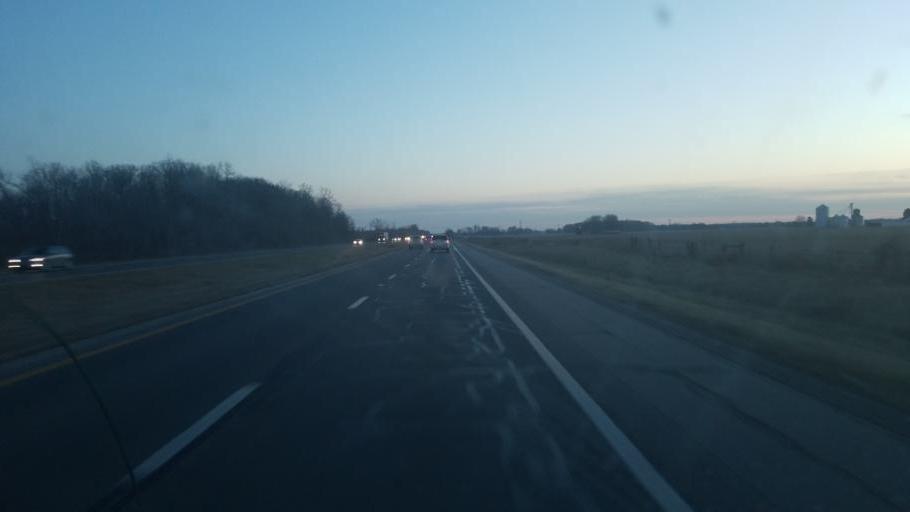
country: US
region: Ohio
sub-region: Marion County
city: Marion
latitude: 40.5169
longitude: -83.0749
